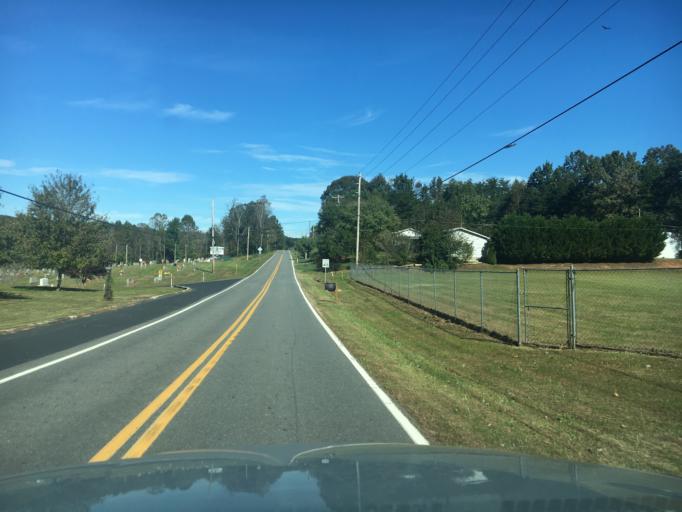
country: US
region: North Carolina
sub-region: Burke County
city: Salem
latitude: 35.7025
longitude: -81.7355
